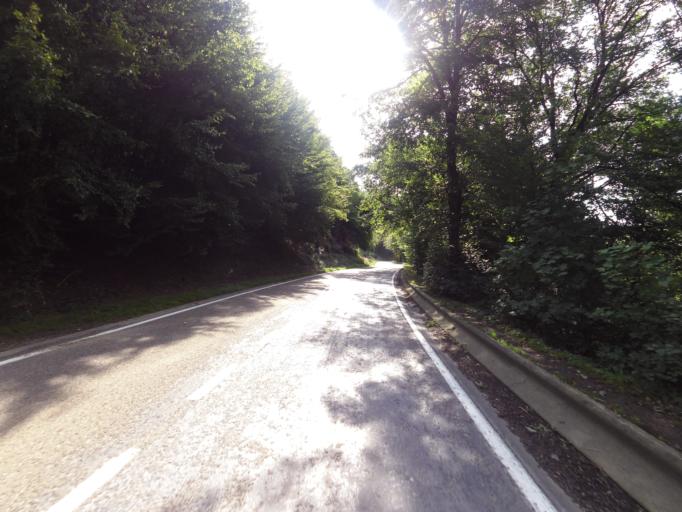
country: BE
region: Wallonia
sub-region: Province du Luxembourg
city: La Roche-en-Ardenne
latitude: 50.1937
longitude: 5.5716
